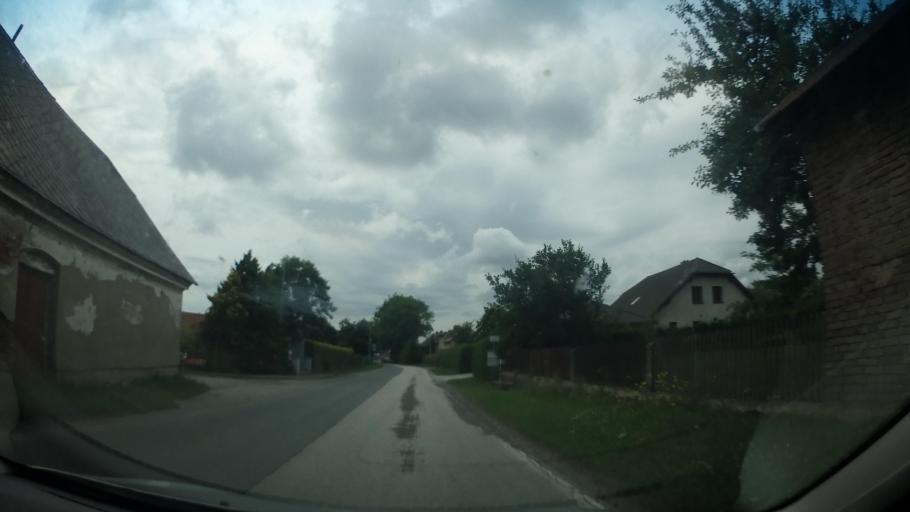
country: CZ
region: Vysocina
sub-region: Okres Zd'ar nad Sazavou
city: Nove Mesto na Morave
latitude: 49.5804
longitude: 16.0777
